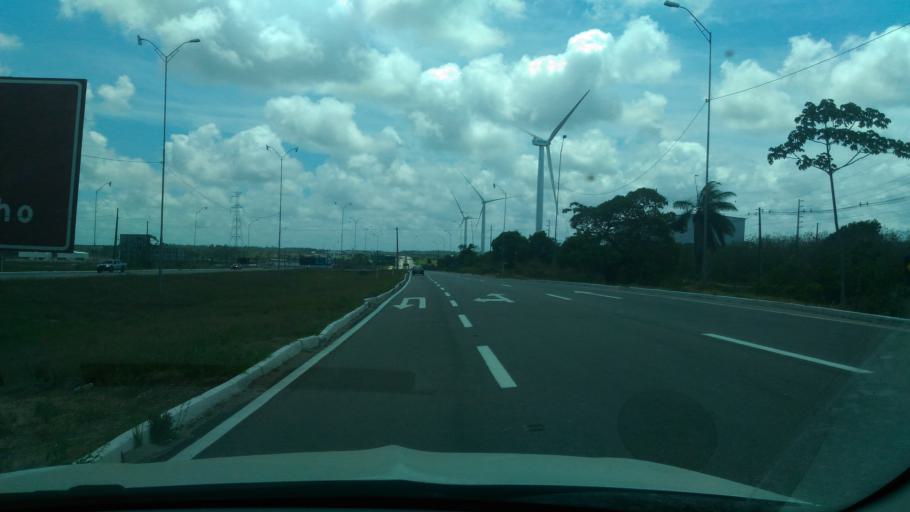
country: BR
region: Paraiba
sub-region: Conde
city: Conde
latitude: -7.2589
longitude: -34.9358
